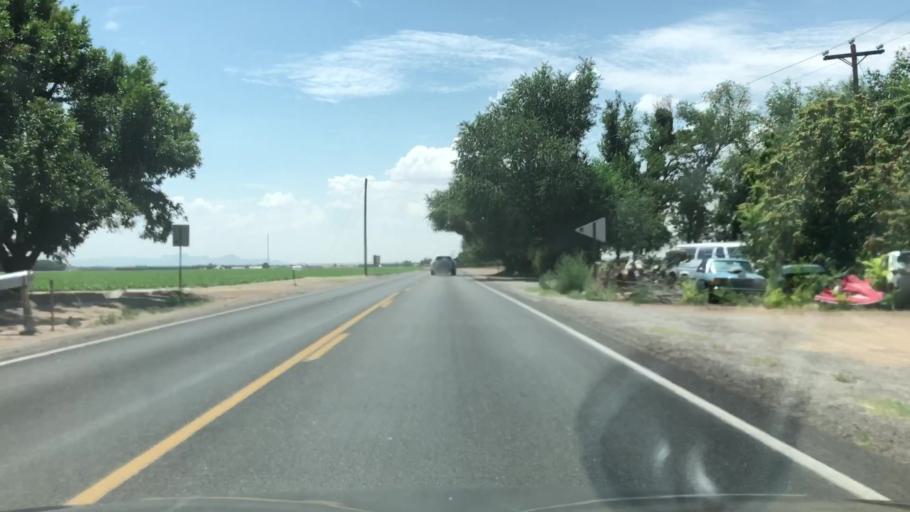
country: US
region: New Mexico
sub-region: Dona Ana County
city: La Union
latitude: 31.9807
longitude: -106.6515
